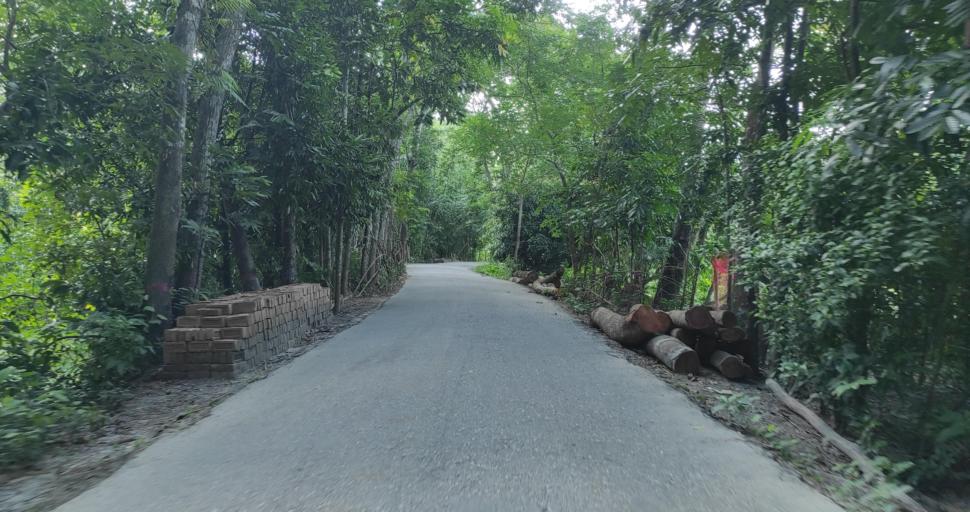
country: BD
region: Barisal
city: Gaurnadi
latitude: 22.8977
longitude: 90.1828
